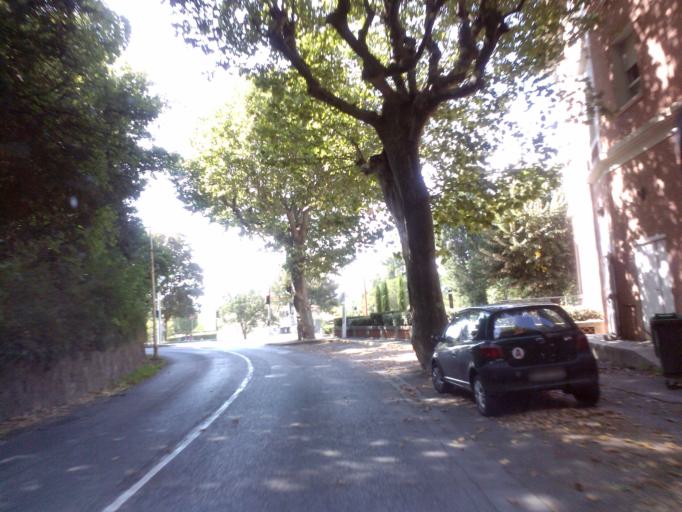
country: FR
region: Provence-Alpes-Cote d'Azur
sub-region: Departement des Alpes-de-Haute-Provence
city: Digne-les-Bains
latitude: 44.0852
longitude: 6.2278
